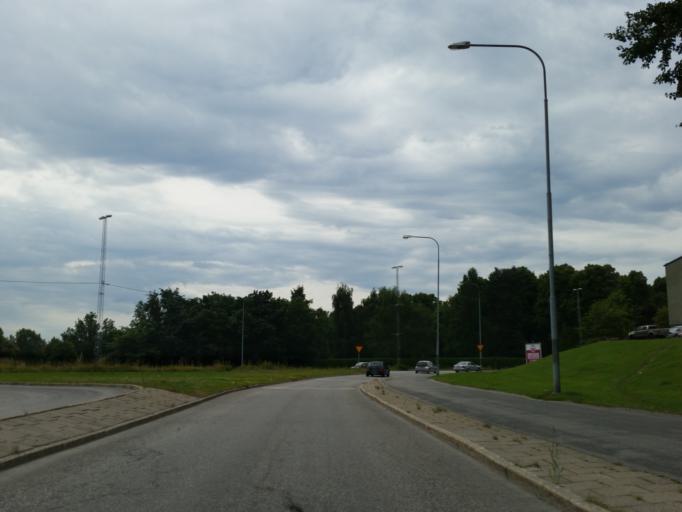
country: SE
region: Stockholm
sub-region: Sodertalje Kommun
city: Soedertaelje
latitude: 59.2031
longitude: 17.6439
